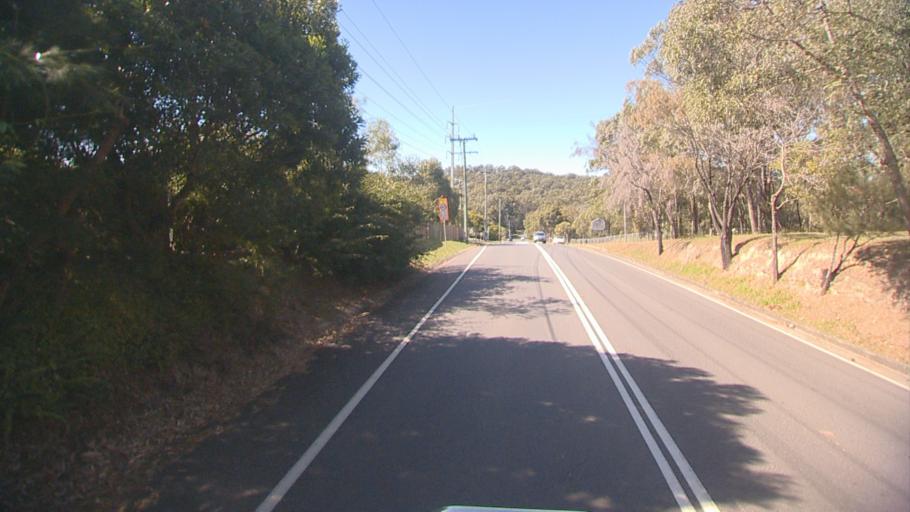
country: AU
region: Queensland
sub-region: Logan
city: Springwood
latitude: -27.6158
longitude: 153.1414
